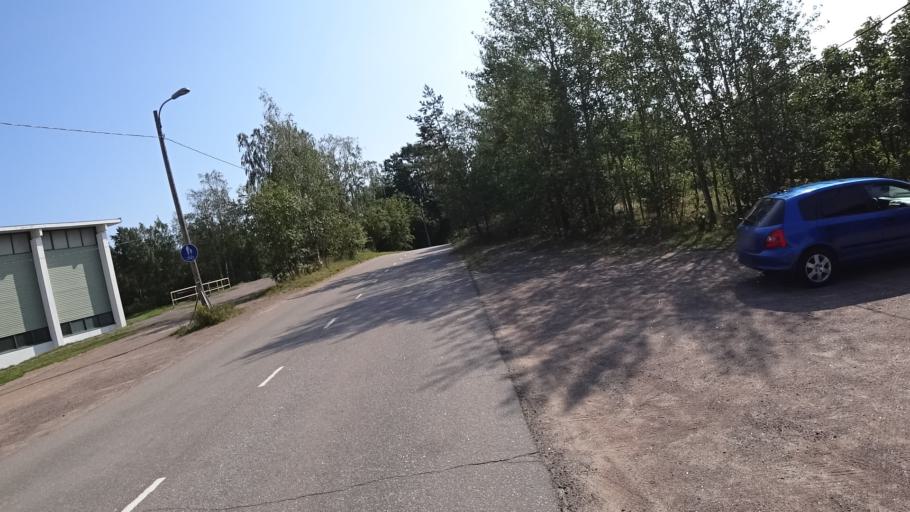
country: FI
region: Kymenlaakso
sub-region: Kotka-Hamina
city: Kotka
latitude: 60.4530
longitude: 26.9371
